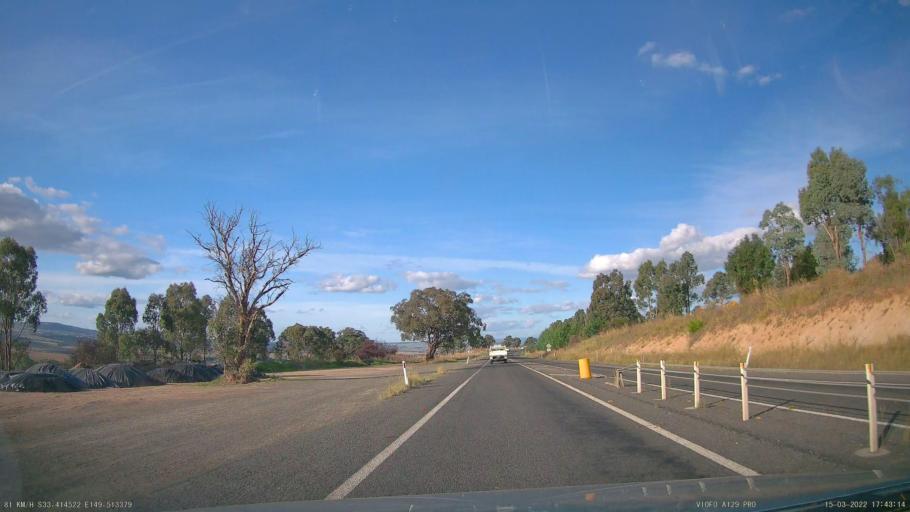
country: AU
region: New South Wales
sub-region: Bathurst Regional
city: Eglinton
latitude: -33.4144
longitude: 149.5136
